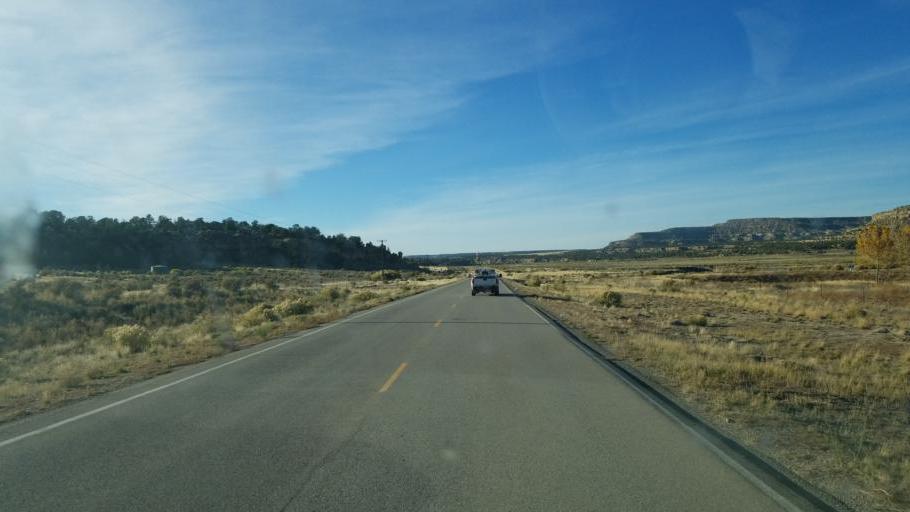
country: US
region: New Mexico
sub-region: San Juan County
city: Bloomfield
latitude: 36.7424
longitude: -107.5790
